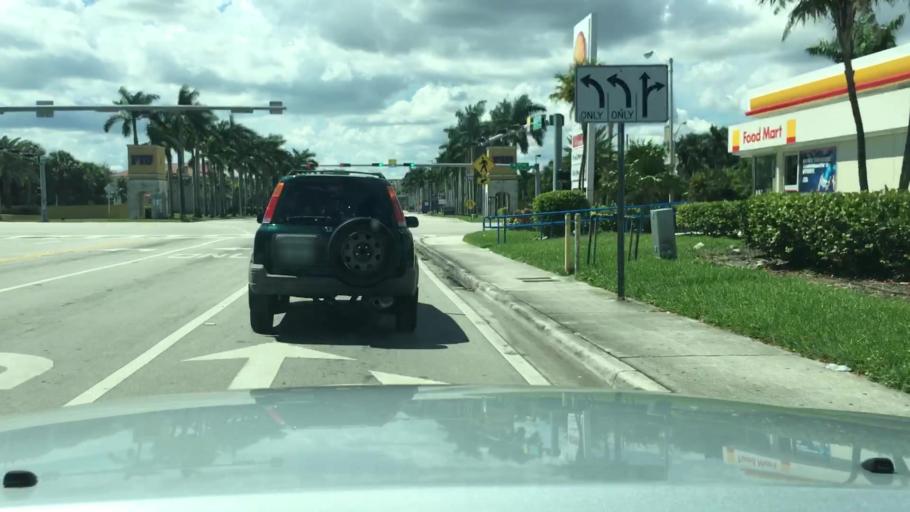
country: US
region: Florida
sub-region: Miami-Dade County
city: University Park
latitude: 25.7544
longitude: -80.3676
